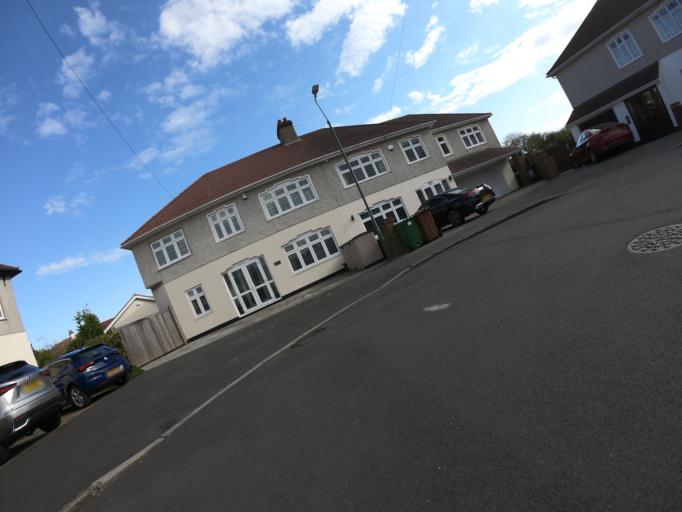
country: GB
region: England
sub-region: Greater London
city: Bexleyheath
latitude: 51.4726
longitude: 0.1347
